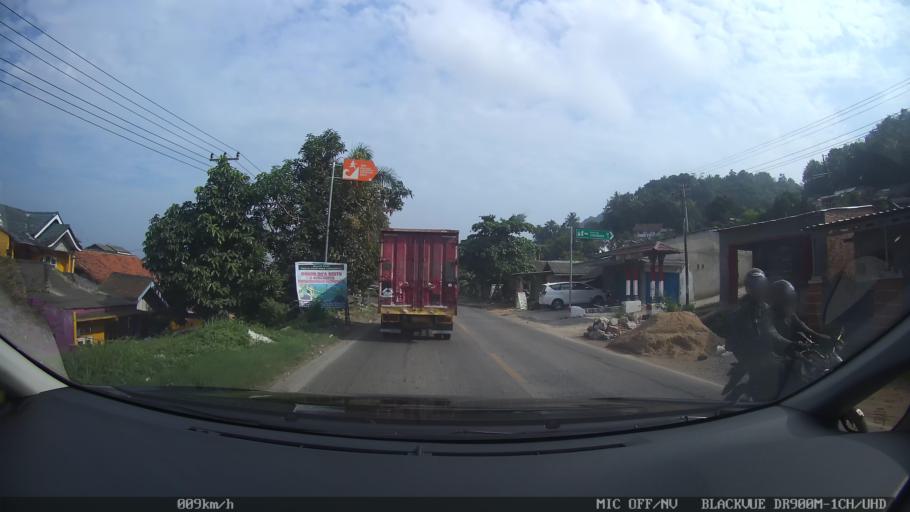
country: ID
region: Lampung
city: Panjang
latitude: -5.4684
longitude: 105.3232
